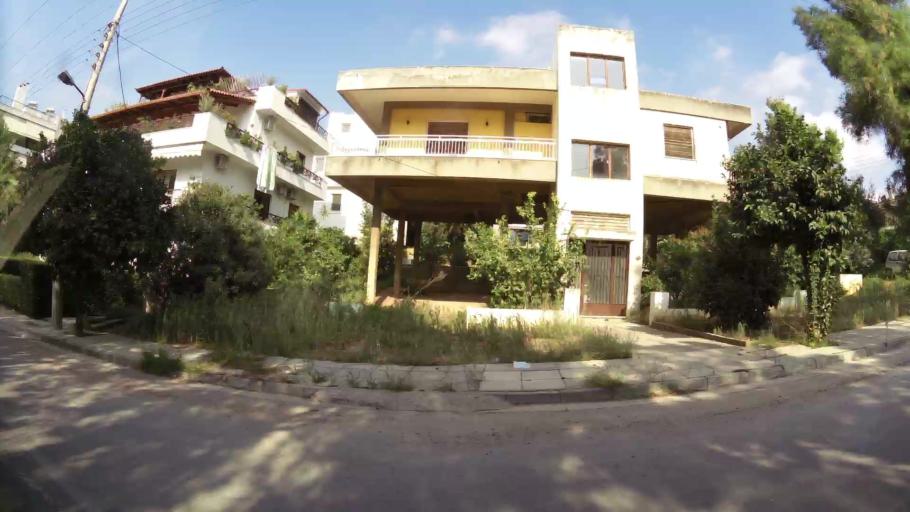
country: GR
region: Attica
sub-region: Nomos Attikis
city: Zografos
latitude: 37.9789
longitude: 23.7907
